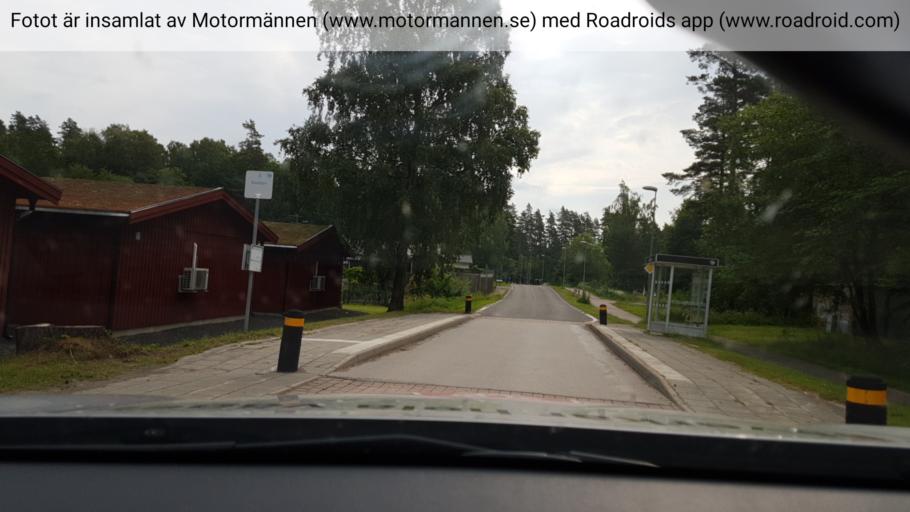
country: SE
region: Vaestra Goetaland
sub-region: Skovde Kommun
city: Skultorp
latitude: 58.3414
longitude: 13.8455
